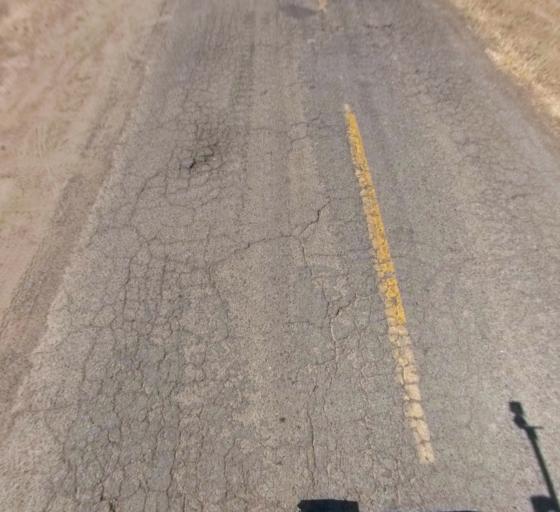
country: US
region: California
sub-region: Madera County
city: Parkwood
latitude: 36.8944
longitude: -120.0285
